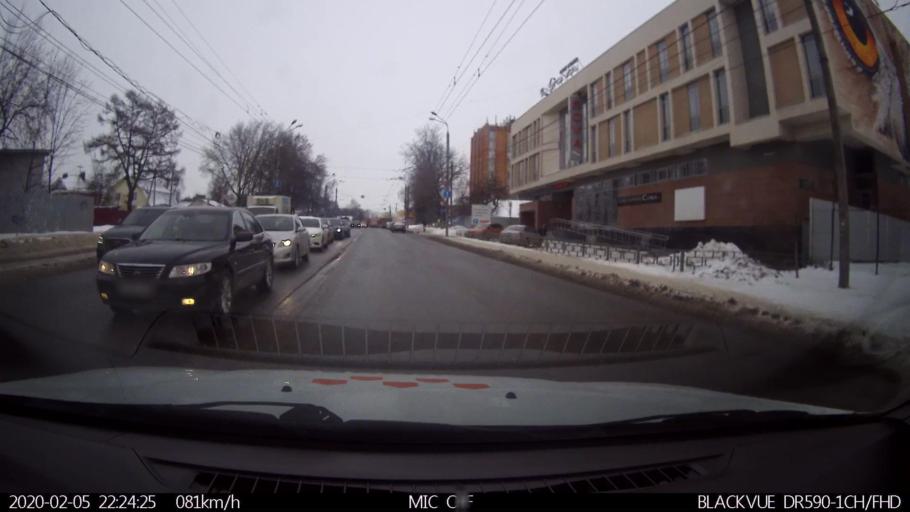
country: RU
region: Nizjnij Novgorod
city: Pervomaysk
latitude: 54.7688
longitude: 44.0450
